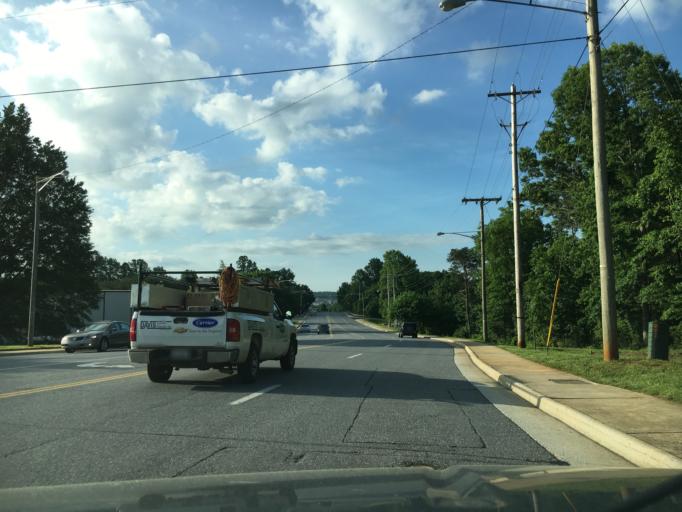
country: US
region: Virginia
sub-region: Bedford County
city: Forest
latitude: 37.3663
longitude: -79.2492
